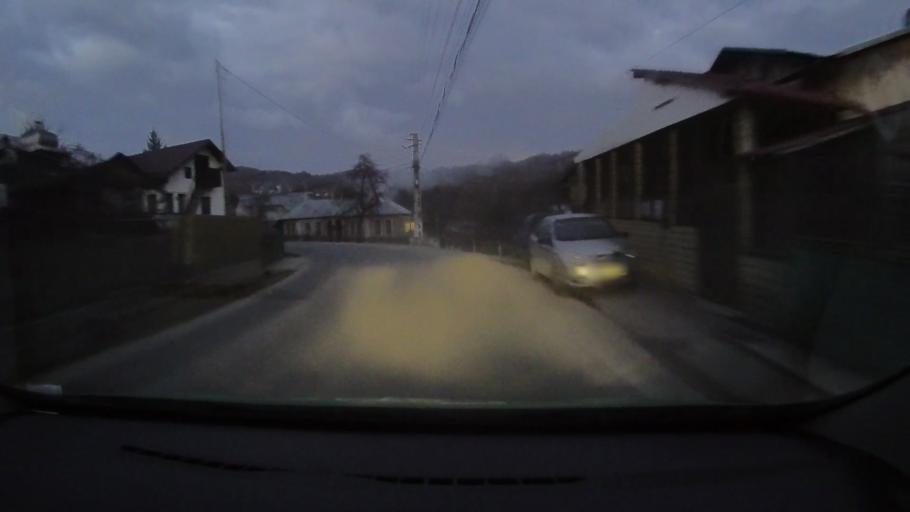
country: RO
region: Prahova
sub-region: Comuna Poiana Campina
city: Poiana Campina
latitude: 45.1210
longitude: 25.6712
